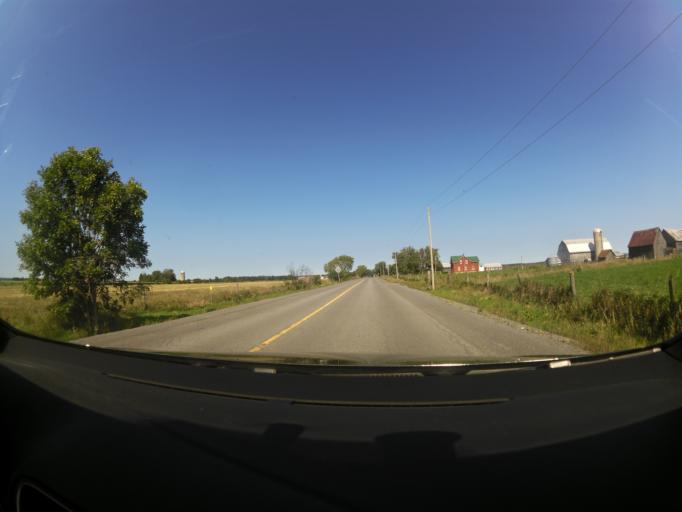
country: CA
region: Ontario
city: Arnprior
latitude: 45.3603
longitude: -76.2435
